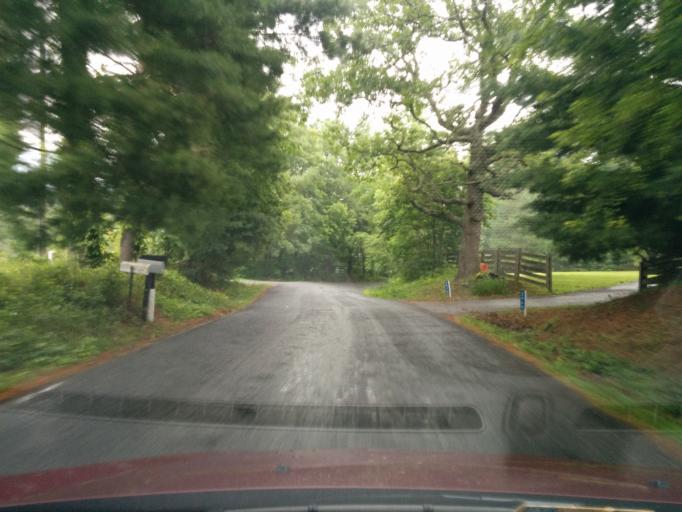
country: US
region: Virginia
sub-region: Rockbridge County
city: East Lexington
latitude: 37.8854
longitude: -79.4389
